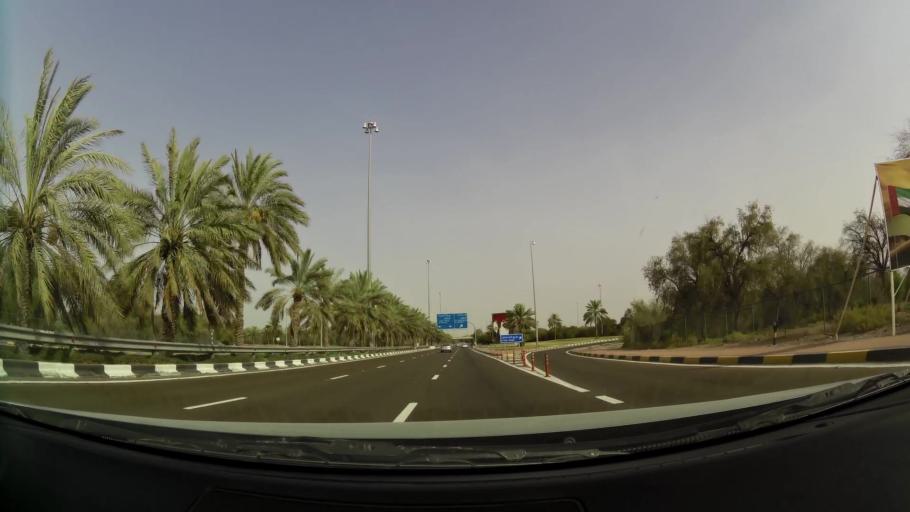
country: AE
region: Abu Dhabi
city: Al Ain
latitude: 24.1875
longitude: 55.5934
